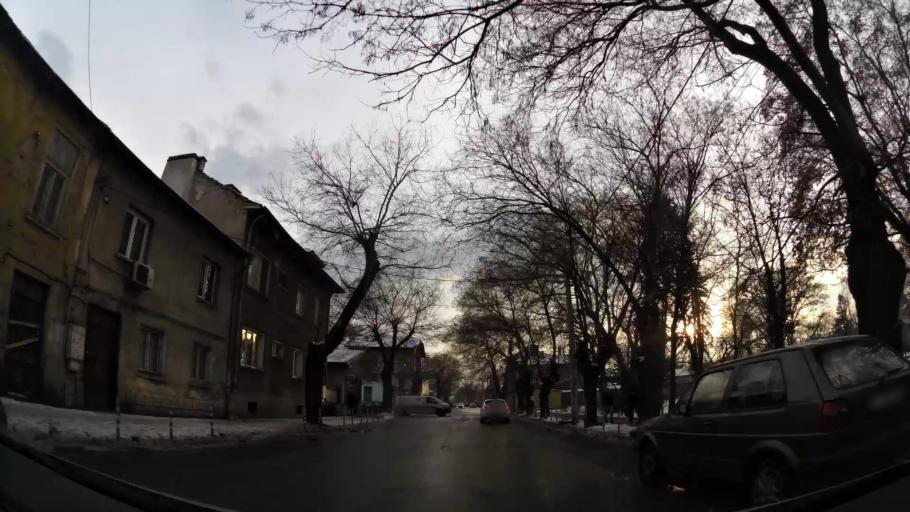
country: BG
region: Sofia-Capital
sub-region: Stolichna Obshtina
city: Sofia
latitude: 42.7191
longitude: 23.3399
